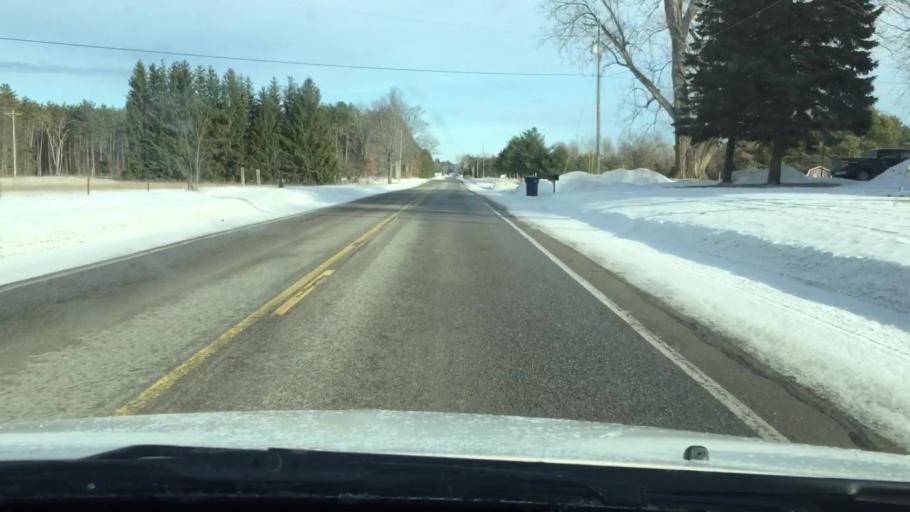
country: US
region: Michigan
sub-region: Kalkaska County
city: Kalkaska
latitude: 44.6406
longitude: -85.1872
